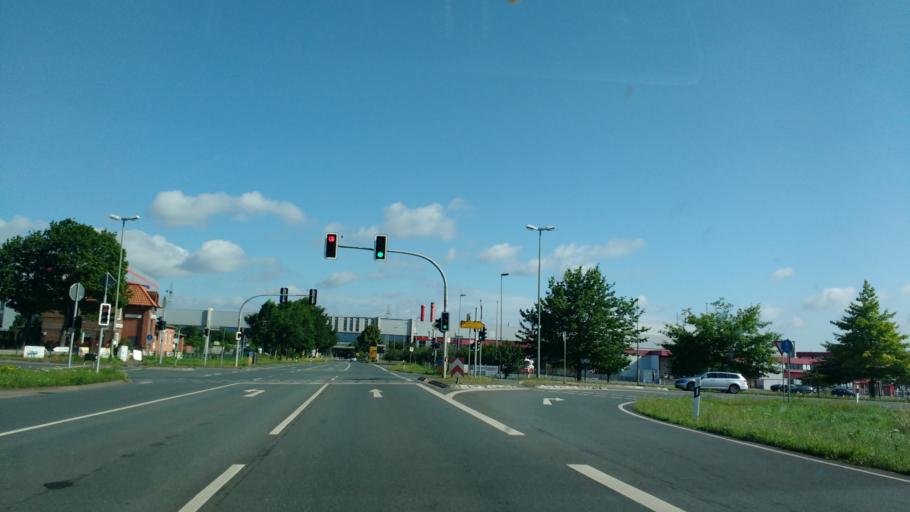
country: DE
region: Lower Saxony
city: Rinteln
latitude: 52.1683
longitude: 9.0854
